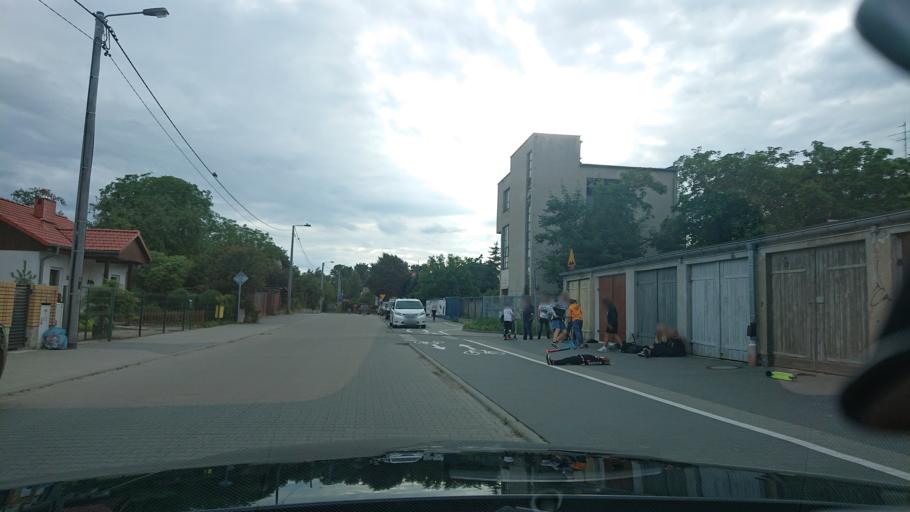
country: PL
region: Greater Poland Voivodeship
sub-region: Powiat gnieznienski
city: Gniezno
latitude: 52.5378
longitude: 17.6166
